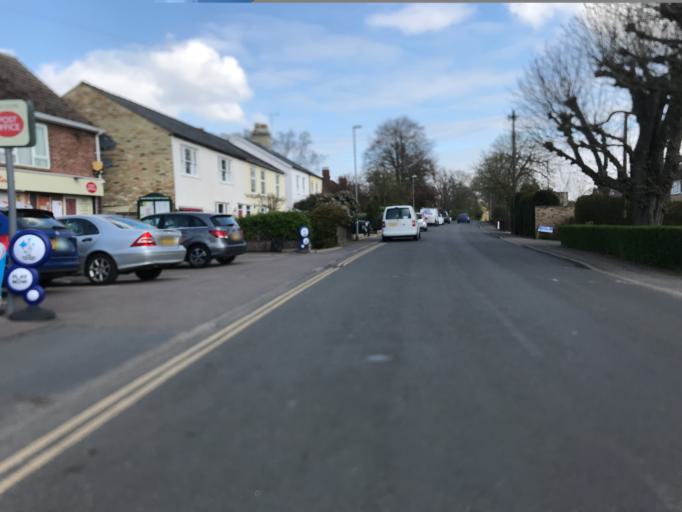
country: GB
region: England
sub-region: Cambridgeshire
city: Sawston
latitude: 52.1507
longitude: 0.1417
